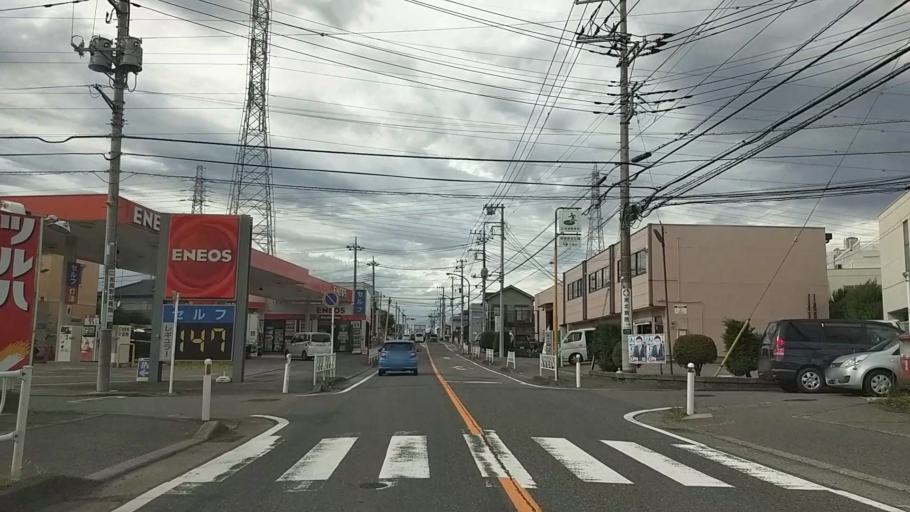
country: JP
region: Tokyo
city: Hachioji
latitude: 35.5894
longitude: 139.3213
